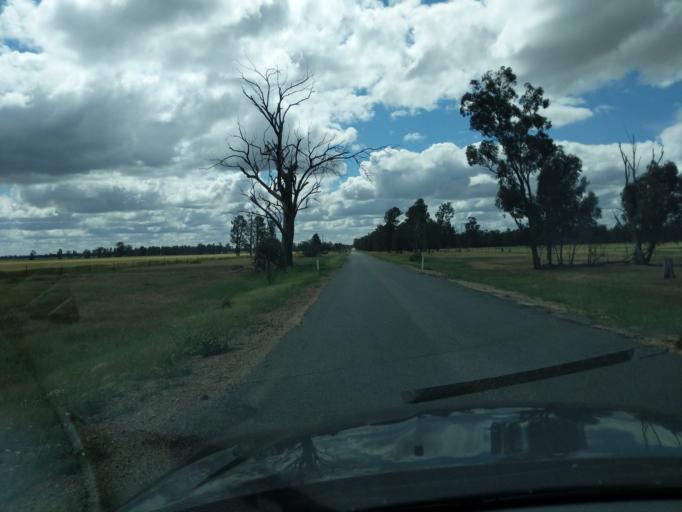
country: AU
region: New South Wales
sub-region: Coolamon
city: Coolamon
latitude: -34.8572
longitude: 146.8986
